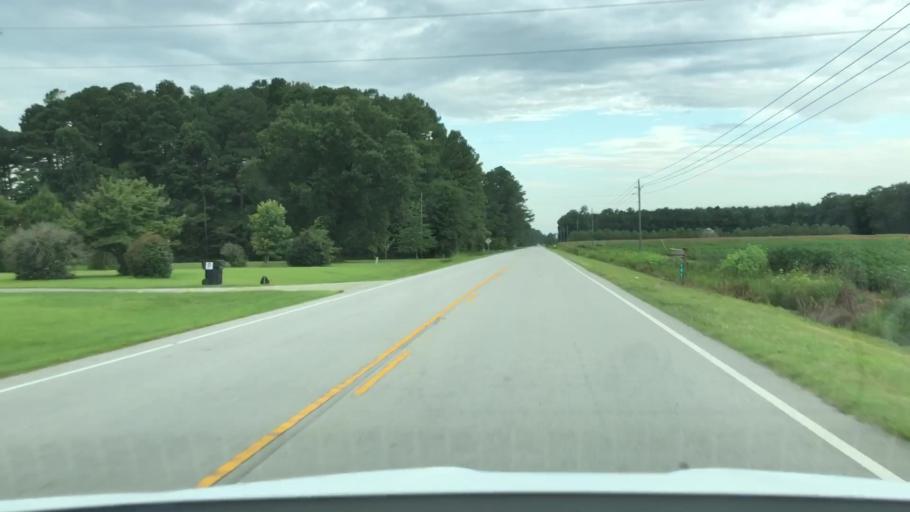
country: US
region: North Carolina
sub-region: Jones County
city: Trenton
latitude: 35.0704
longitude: -77.3738
